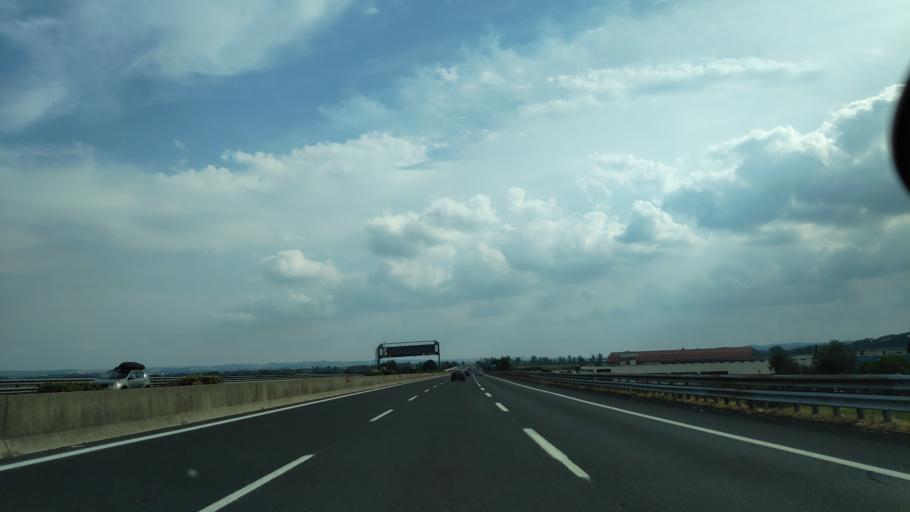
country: IT
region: Latium
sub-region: Citta metropolitana di Roma Capitale
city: Fiano Romano
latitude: 42.1473
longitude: 12.6236
